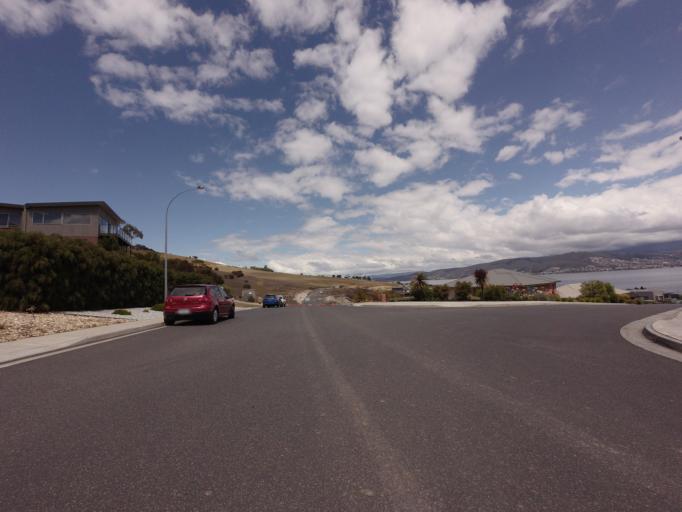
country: AU
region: Tasmania
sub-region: Clarence
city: Howrah
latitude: -42.9133
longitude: 147.4211
